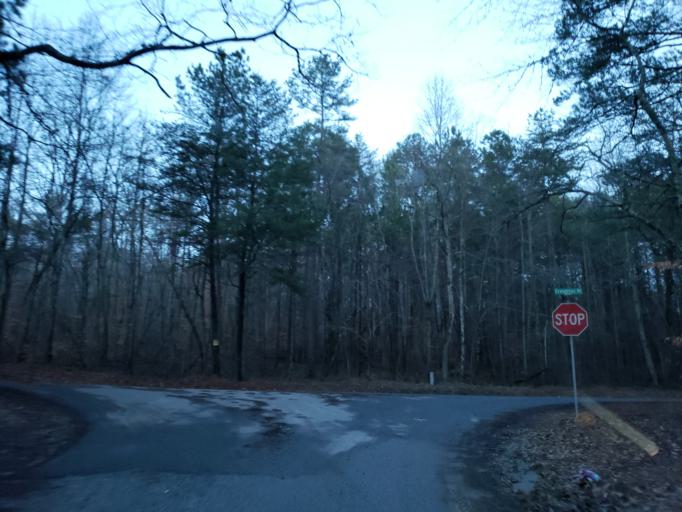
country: US
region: Georgia
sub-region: Cherokee County
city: Ball Ground
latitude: 34.2917
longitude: -84.3012
